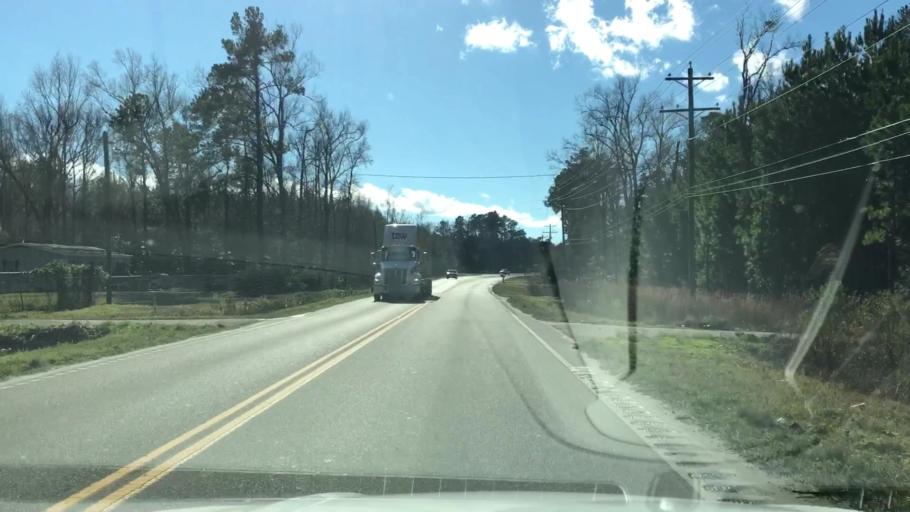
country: US
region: South Carolina
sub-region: Dorchester County
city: Summerville
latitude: 33.0863
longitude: -80.2021
